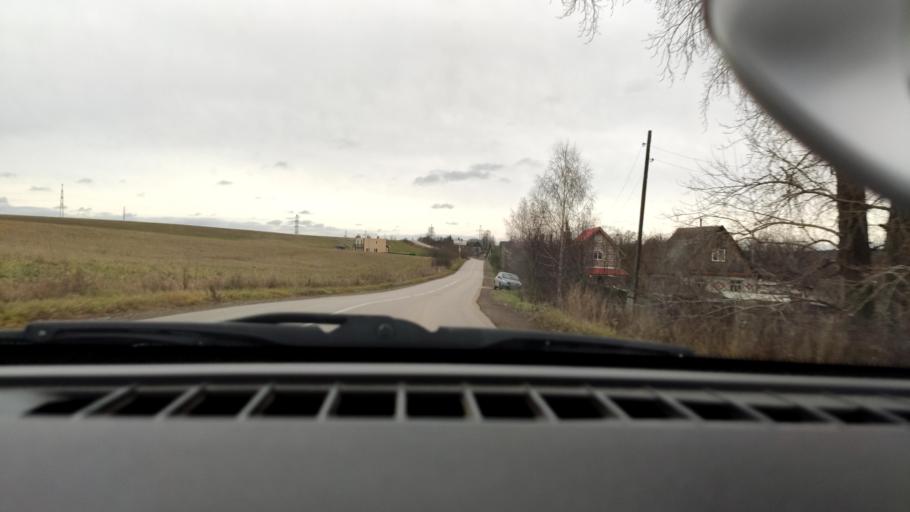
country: RU
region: Perm
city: Ferma
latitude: 57.9217
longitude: 56.3283
